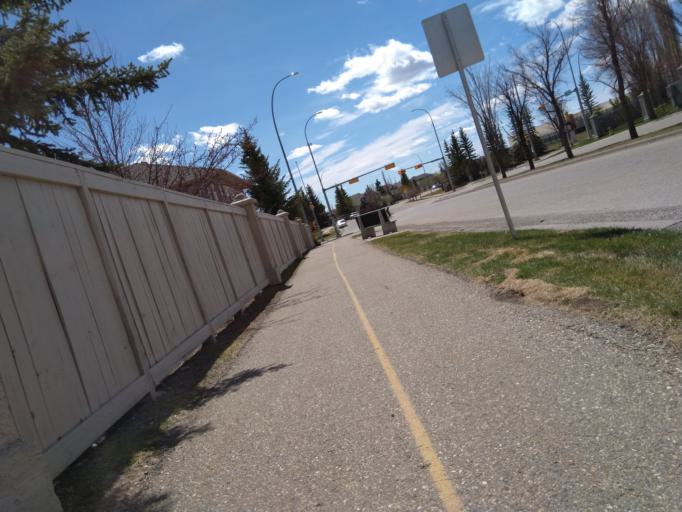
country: CA
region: Alberta
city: Calgary
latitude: 51.1257
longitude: -114.2432
